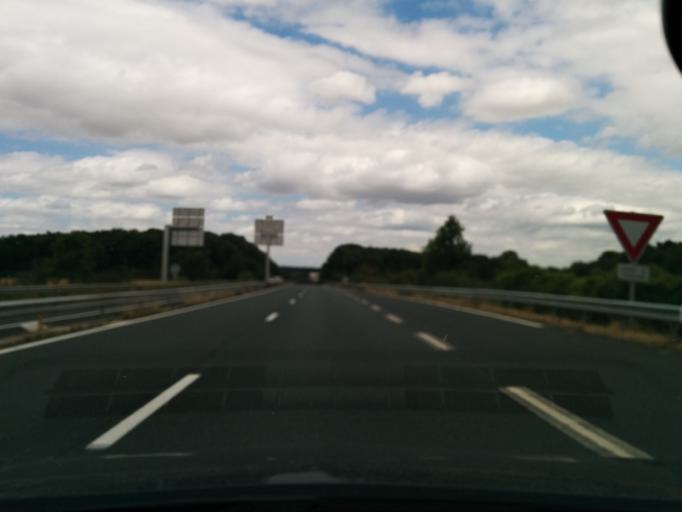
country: FR
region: Centre
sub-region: Departement de l'Indre
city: Saint-Marcel
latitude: 46.6186
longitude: 1.5420
